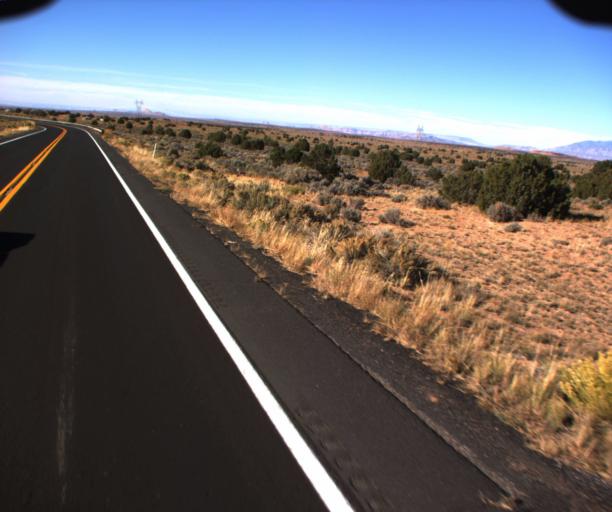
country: US
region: Arizona
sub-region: Coconino County
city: Kaibito
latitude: 36.6121
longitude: -110.9232
